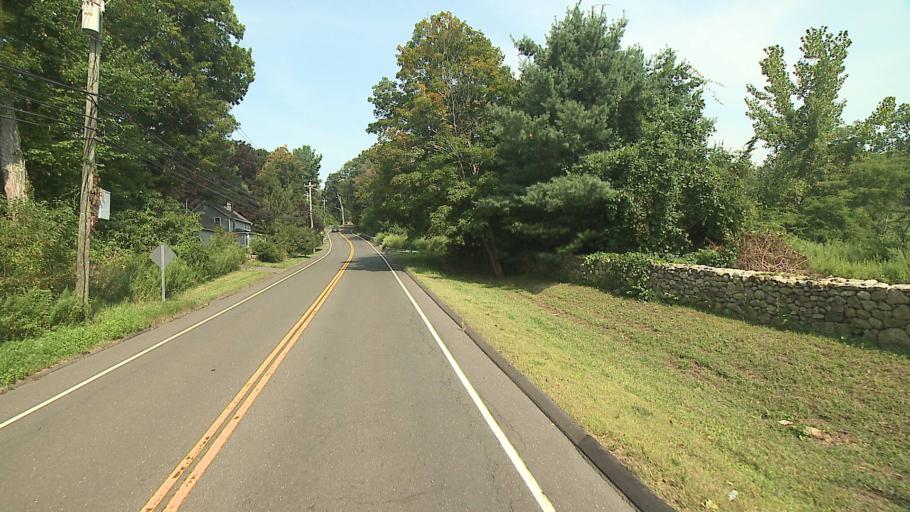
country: US
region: Connecticut
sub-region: Fairfield County
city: Georgetown
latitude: 41.2464
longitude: -73.4152
